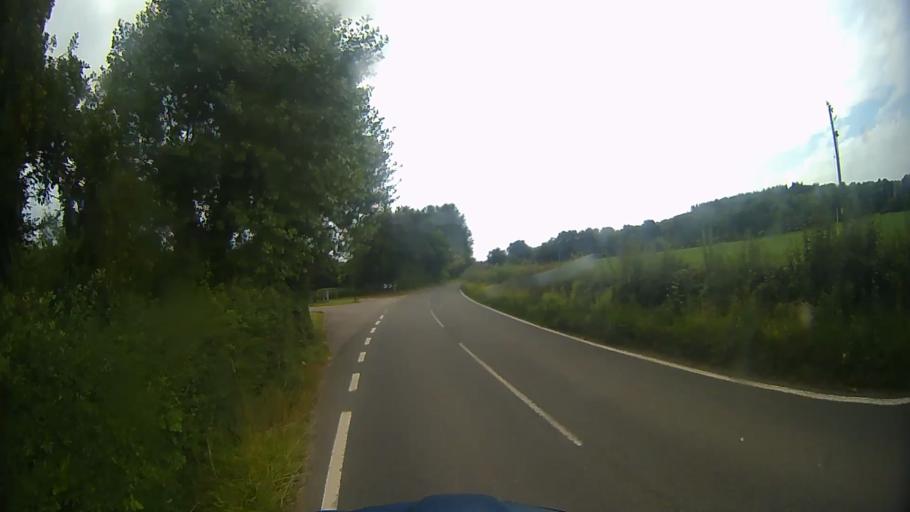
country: GB
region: England
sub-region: Hampshire
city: Kingsley
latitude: 51.1769
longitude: -0.8696
